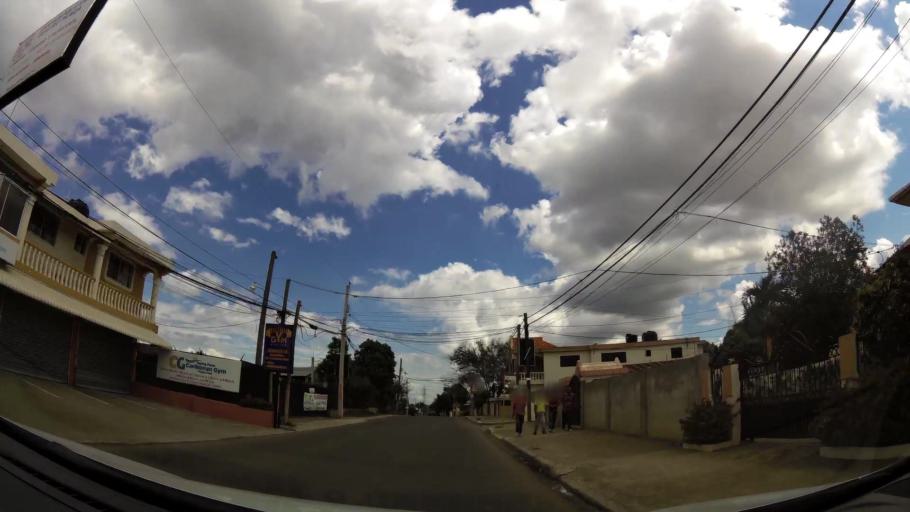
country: DO
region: Santiago
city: Santiago de los Caballeros
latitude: 19.4035
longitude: -70.6588
